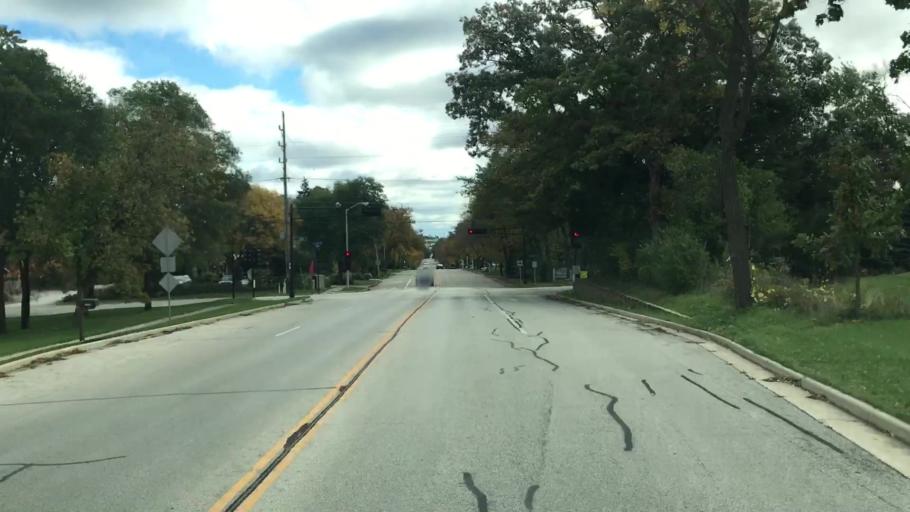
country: US
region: Wisconsin
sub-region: Waukesha County
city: Elm Grove
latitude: 43.0454
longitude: -88.0679
